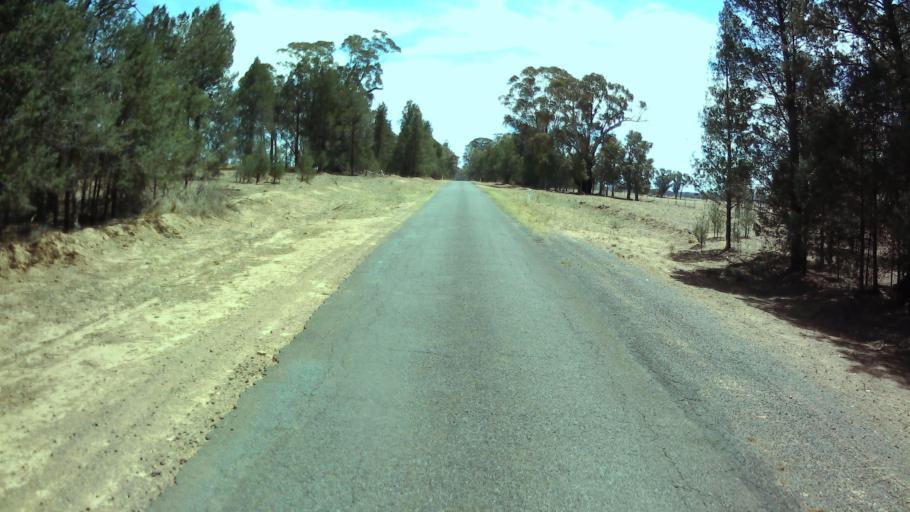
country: AU
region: New South Wales
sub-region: Weddin
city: Grenfell
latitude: -33.7595
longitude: 148.2054
